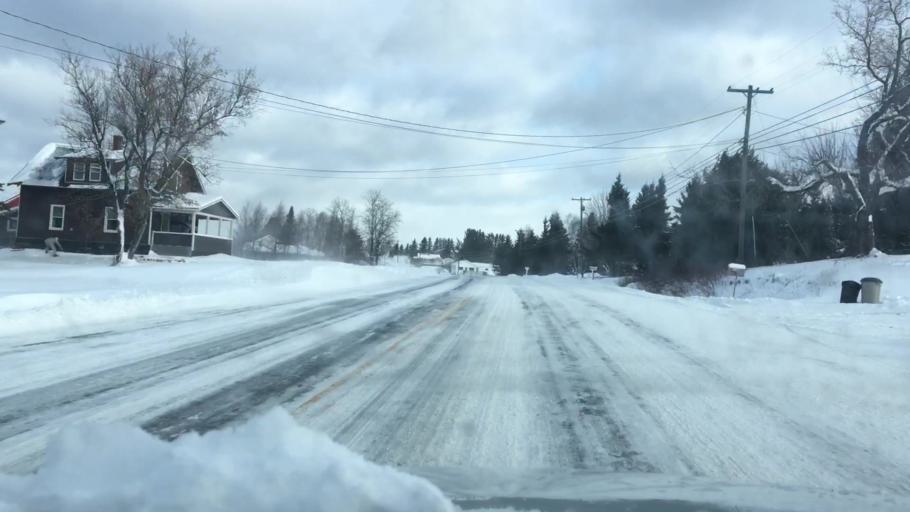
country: US
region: Maine
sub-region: Aroostook County
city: Caribou
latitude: 46.9852
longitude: -68.0313
